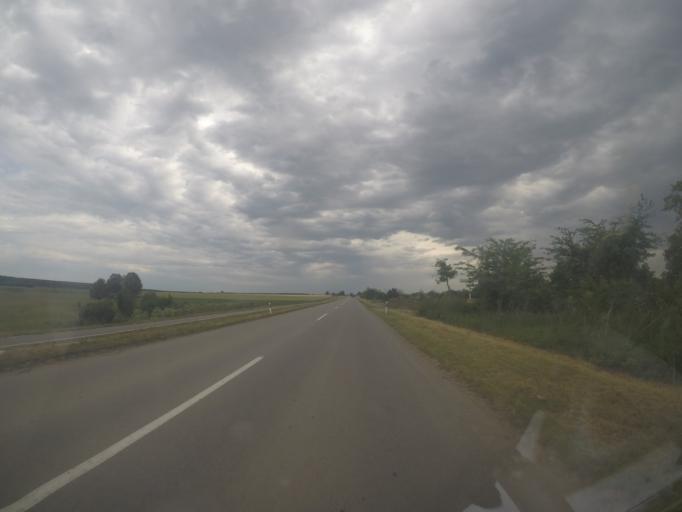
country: RS
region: Autonomna Pokrajina Vojvodina
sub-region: Juznobanatski Okrug
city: Opovo
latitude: 45.0639
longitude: 20.4365
